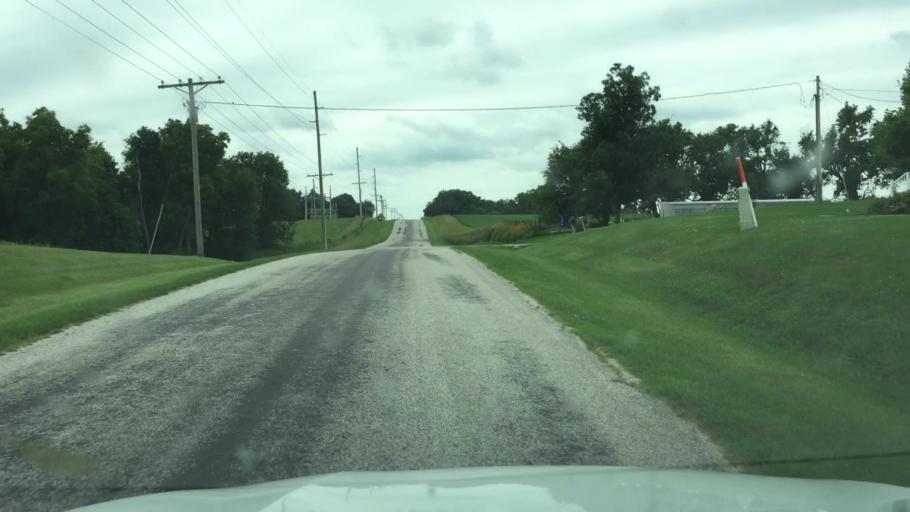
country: US
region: Illinois
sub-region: Hancock County
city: Carthage
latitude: 40.2984
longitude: -91.0832
